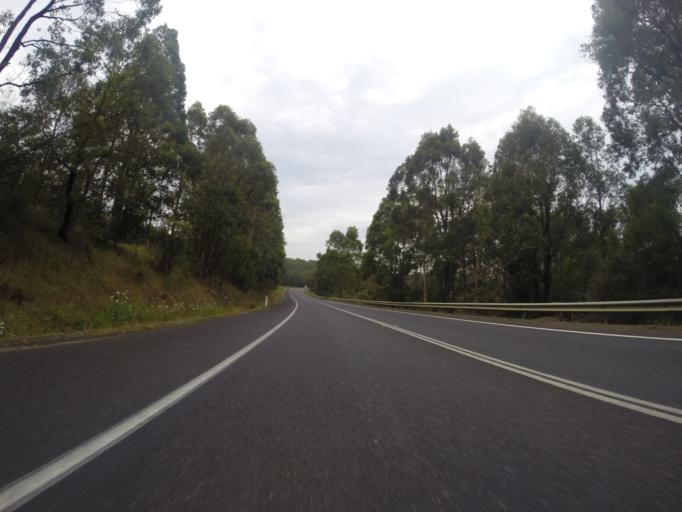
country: AU
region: New South Wales
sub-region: Eurobodalla
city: Batemans Bay
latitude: -35.6801
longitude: 150.2066
